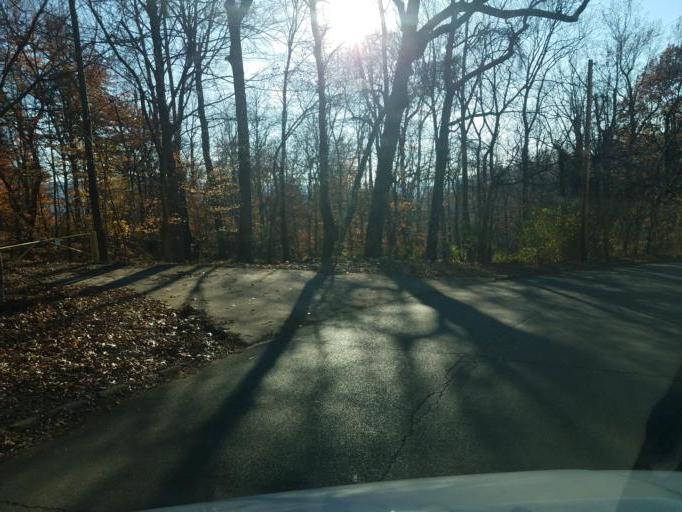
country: US
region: Ohio
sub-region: Scioto County
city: Portsmouth
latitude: 38.7531
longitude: -82.9855
